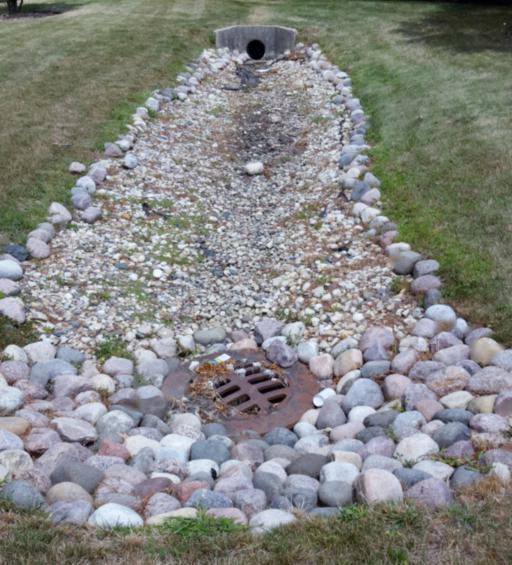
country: US
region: Illinois
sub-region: Cook County
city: Northfield
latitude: 42.1000
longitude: -87.7983
